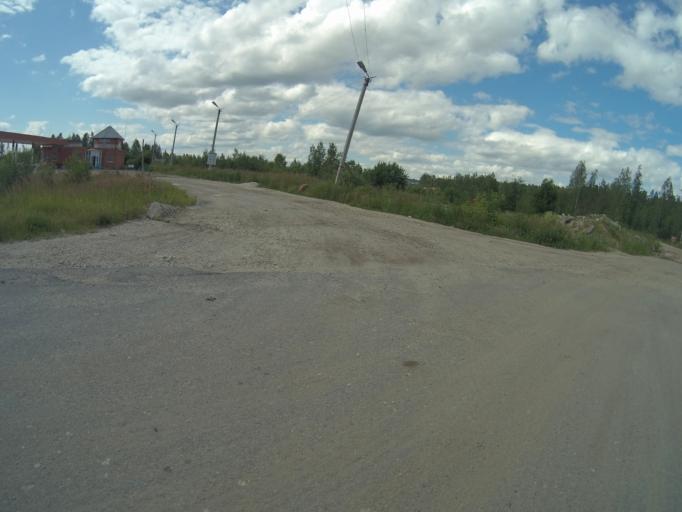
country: RU
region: Vladimir
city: Raduzhnyy
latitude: 56.0722
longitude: 40.2803
